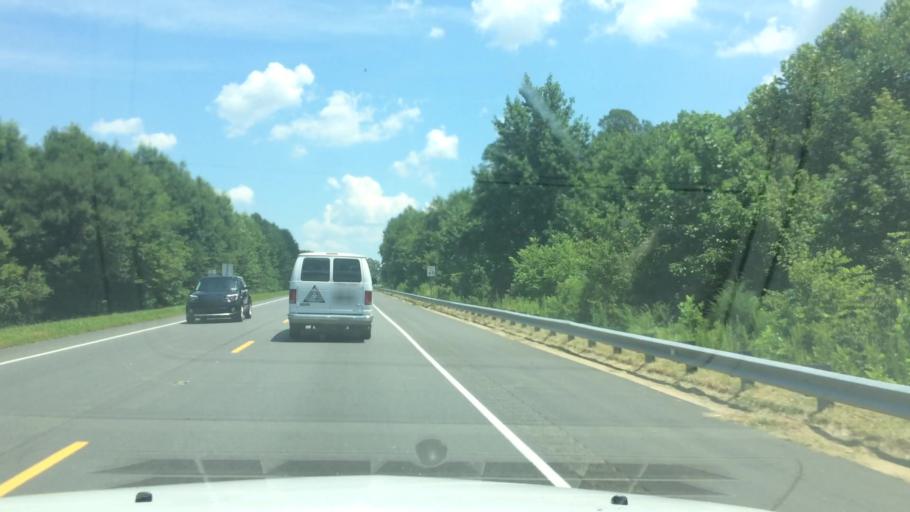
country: US
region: North Carolina
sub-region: Iredell County
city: Statesville
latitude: 35.8027
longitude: -80.9502
